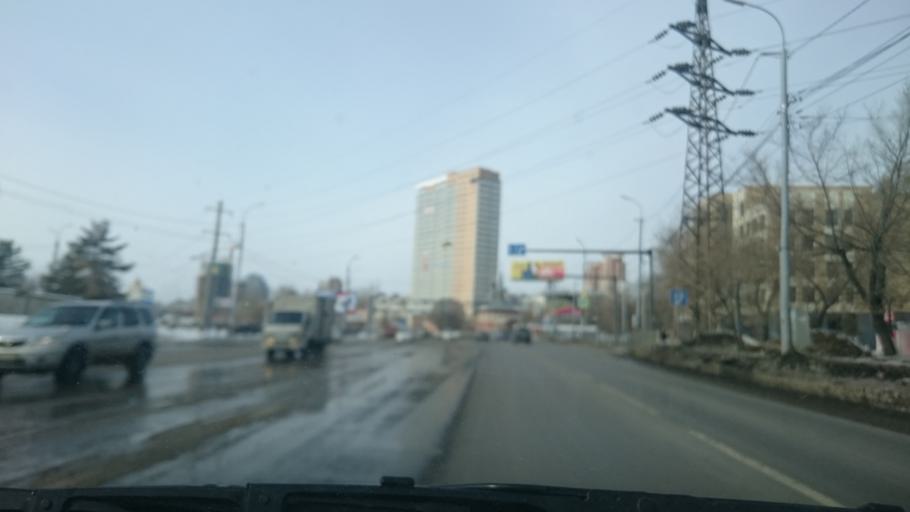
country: RU
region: Khabarovsk Krai
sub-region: Khabarovskiy Rayon
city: Khabarovsk
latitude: 48.4609
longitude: 135.0878
